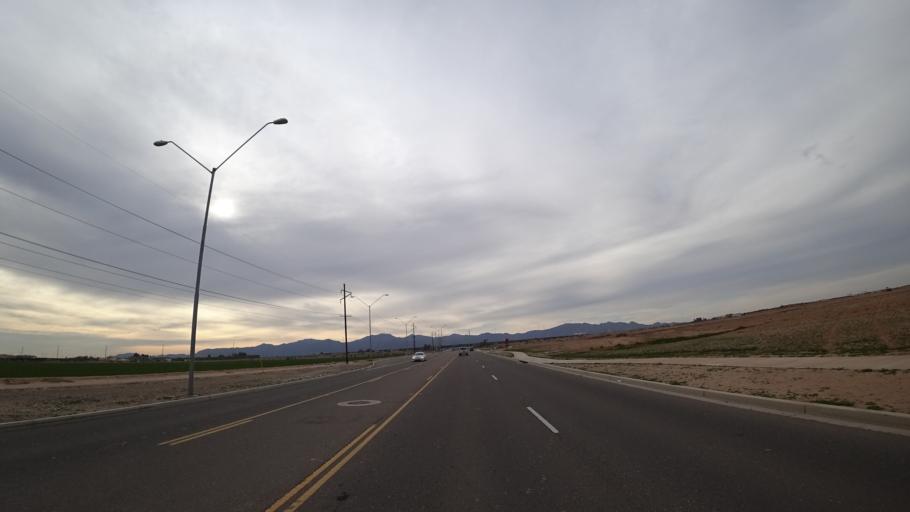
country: US
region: Arizona
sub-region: Maricopa County
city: Citrus Park
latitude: 33.5954
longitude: -112.4104
